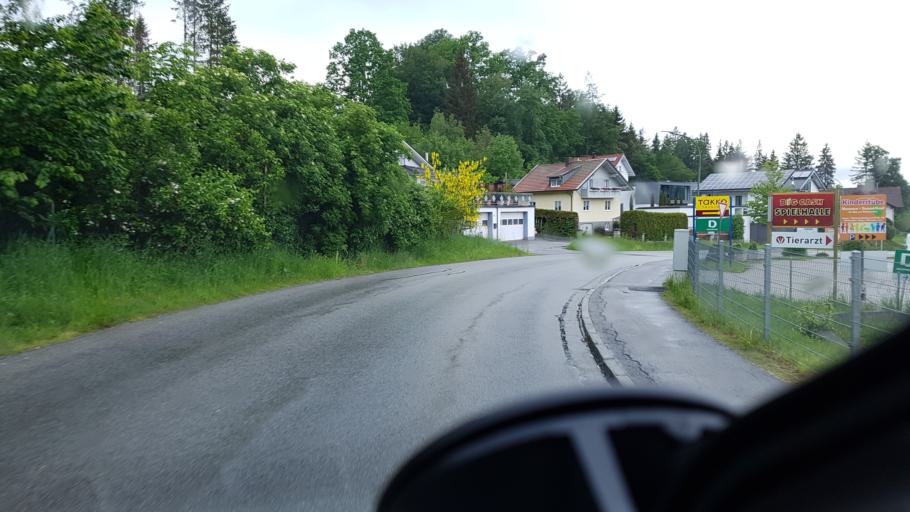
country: DE
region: Bavaria
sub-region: Lower Bavaria
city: Waldkirchen
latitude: 48.7225
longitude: 13.6124
